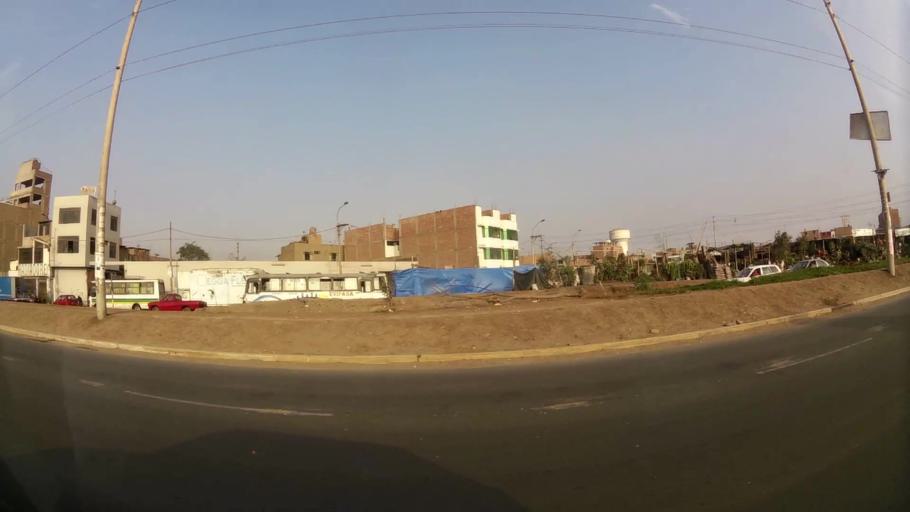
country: PE
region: Lima
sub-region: Lima
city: Independencia
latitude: -11.9880
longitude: -77.1039
